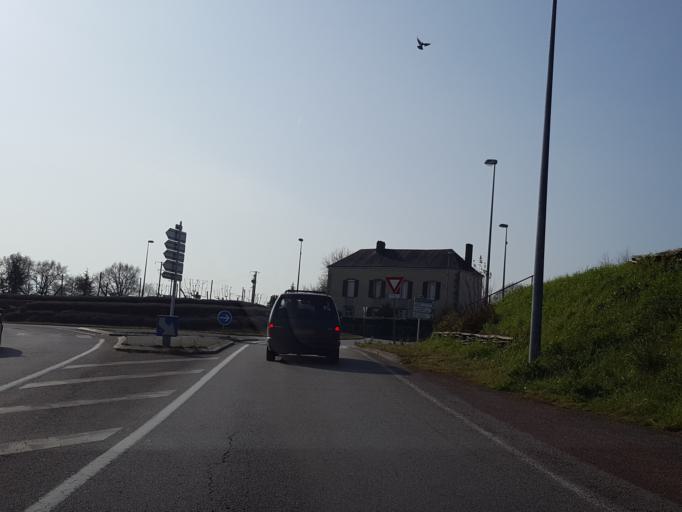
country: FR
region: Pays de la Loire
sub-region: Departement de la Vendee
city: Rocheserviere
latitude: 46.9332
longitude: -1.5144
